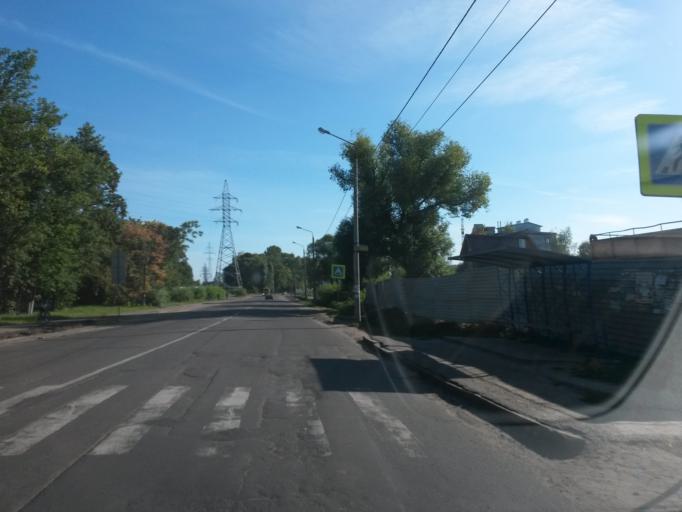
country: RU
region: Jaroslavl
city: Yaroslavl
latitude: 57.5891
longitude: 39.8769
